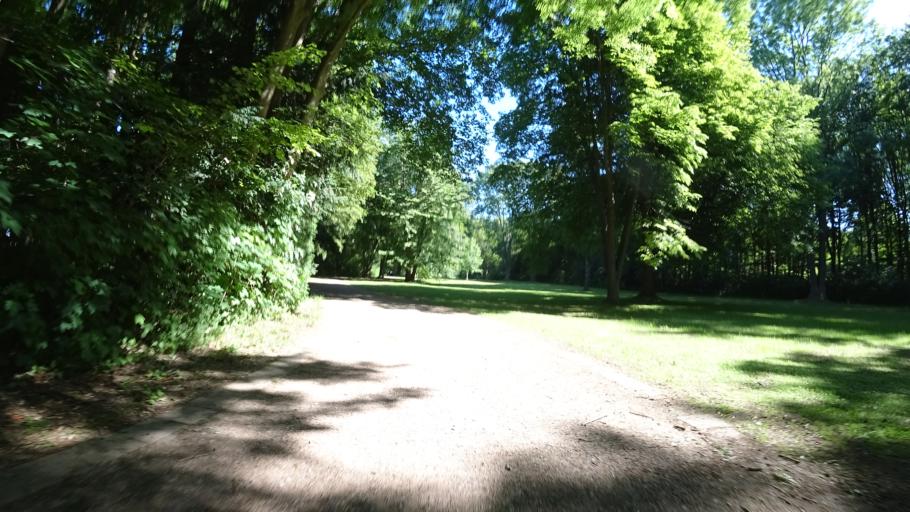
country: DE
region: North Rhine-Westphalia
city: Erwitte
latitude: 51.6339
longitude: 8.3531
